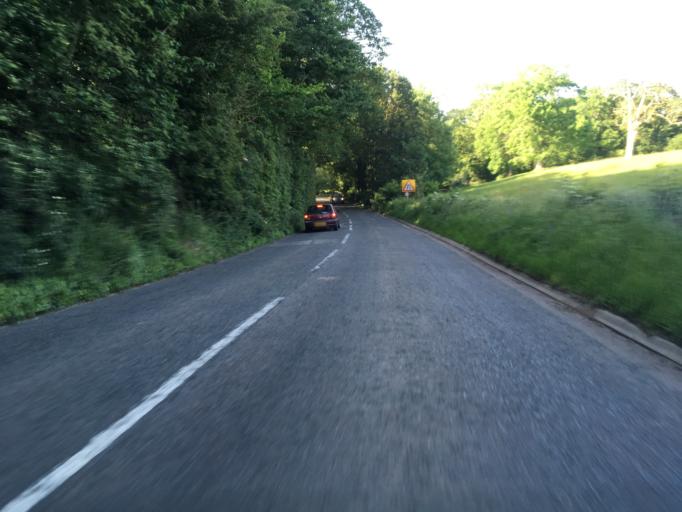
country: GB
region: England
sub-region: Oxfordshire
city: Charlbury
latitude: 51.9155
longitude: -1.4466
